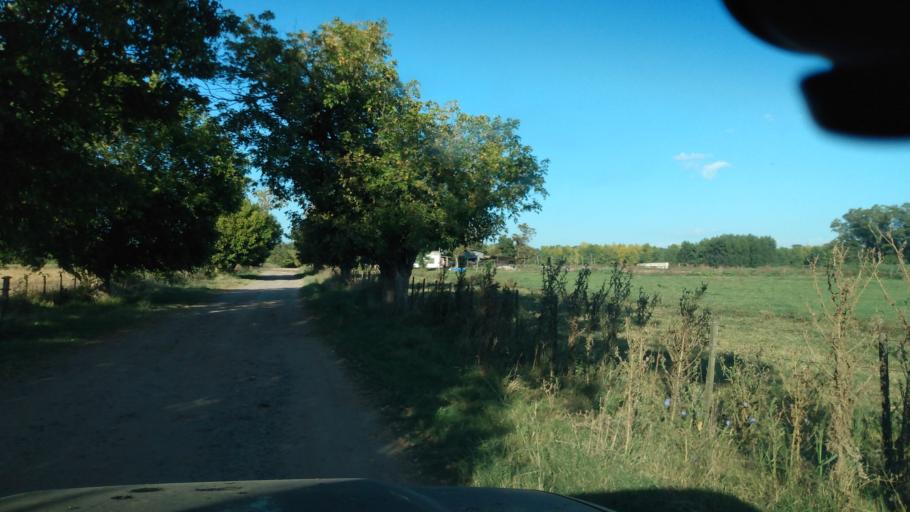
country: AR
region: Buenos Aires
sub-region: Partido de Lujan
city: Lujan
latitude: -34.5879
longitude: -59.0697
